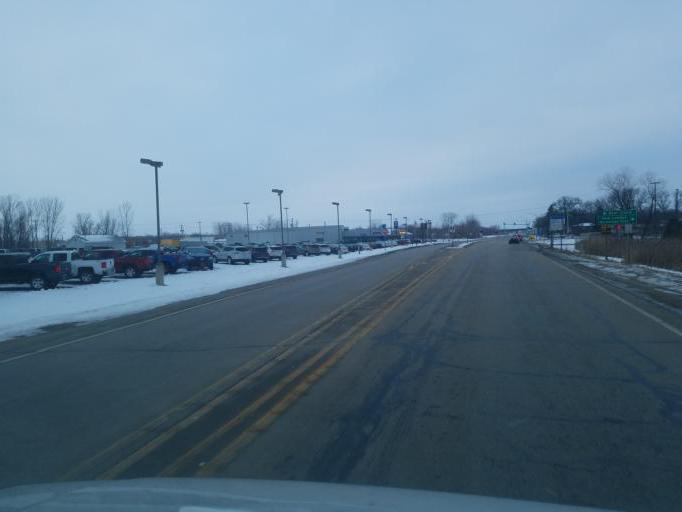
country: US
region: Wisconsin
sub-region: Waupaca County
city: New London
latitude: 44.4025
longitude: -88.7459
